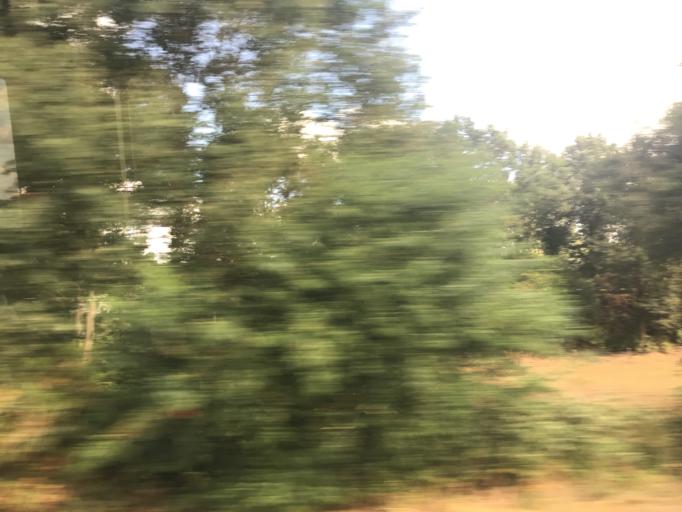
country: NL
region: Gelderland
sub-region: Gemeente Lochem
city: Laren
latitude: 52.2805
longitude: 6.4005
